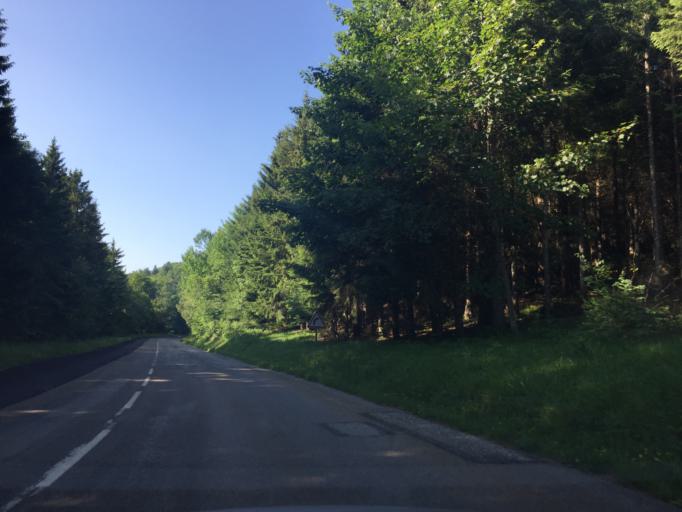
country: FR
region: Rhone-Alpes
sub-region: Departement de la Drome
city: Saint-Laurent-en-Royans
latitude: 44.9949
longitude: 5.3639
